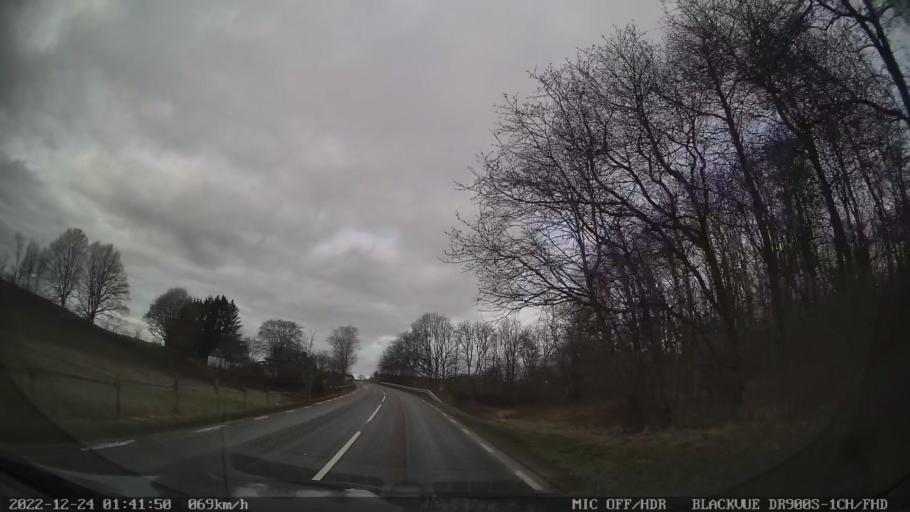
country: SE
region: Skane
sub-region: Tomelilla Kommun
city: Tomelilla
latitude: 55.5974
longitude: 14.0860
